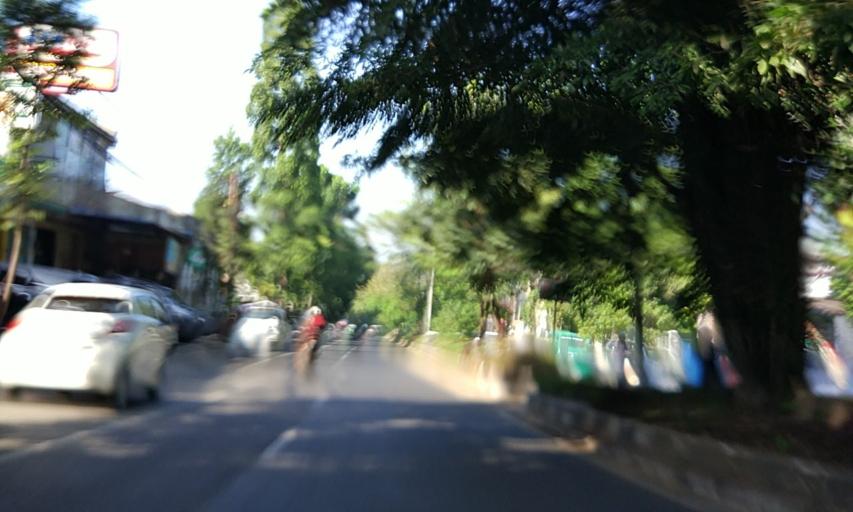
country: ID
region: West Java
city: Bandung
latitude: -6.8797
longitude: 107.6164
